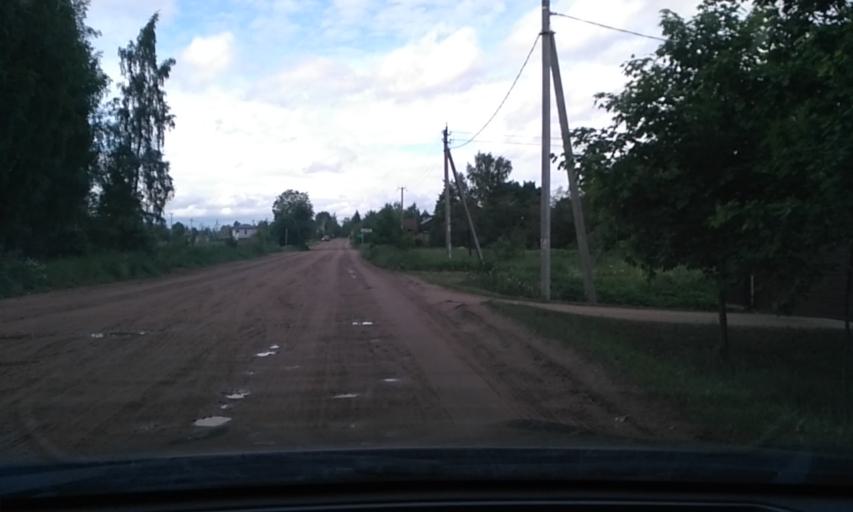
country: RU
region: Leningrad
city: Otradnoye
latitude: 59.7922
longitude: 30.7946
